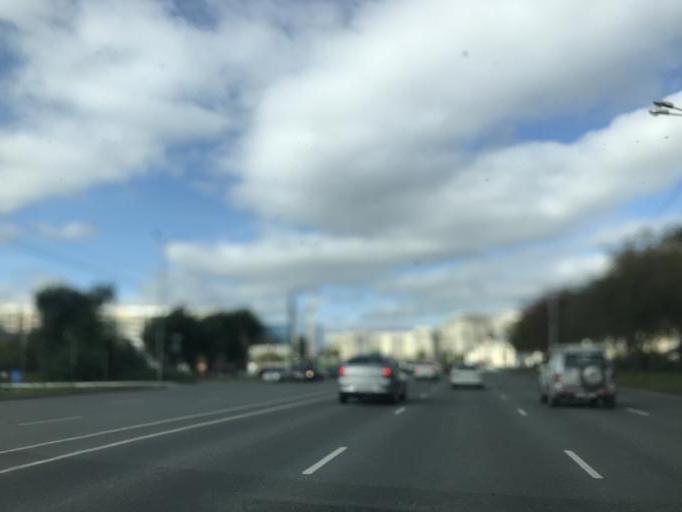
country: RU
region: Chelyabinsk
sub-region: Gorod Chelyabinsk
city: Chelyabinsk
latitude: 55.1772
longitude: 61.3754
